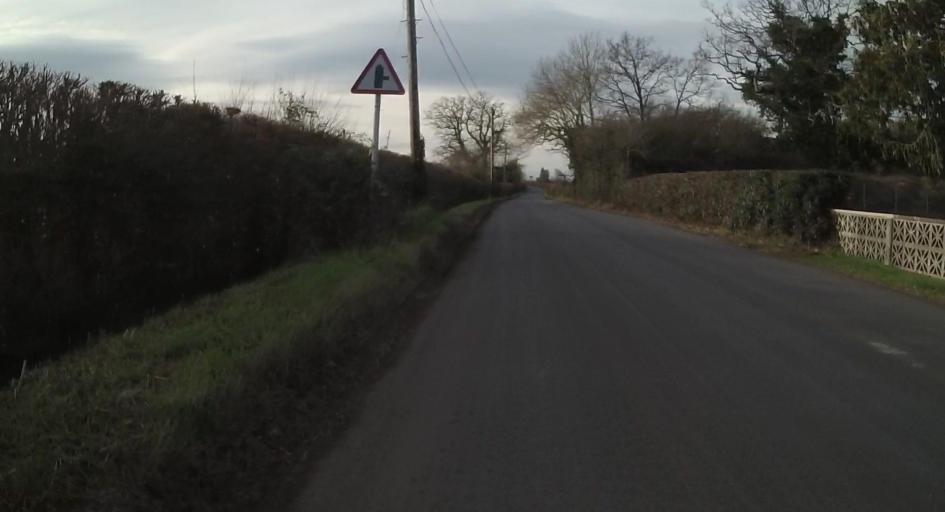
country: GB
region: England
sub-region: West Berkshire
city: Stratfield Mortimer
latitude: 51.4036
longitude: -1.0313
